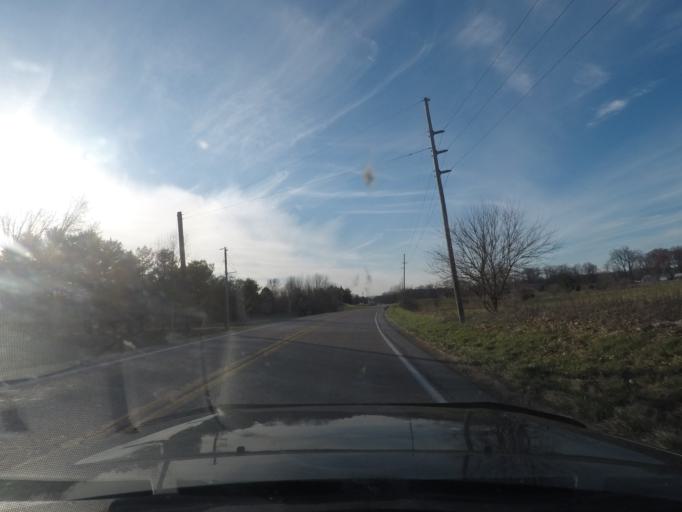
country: US
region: Indiana
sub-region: Saint Joseph County
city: Walkerton
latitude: 41.4485
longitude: -86.4404
